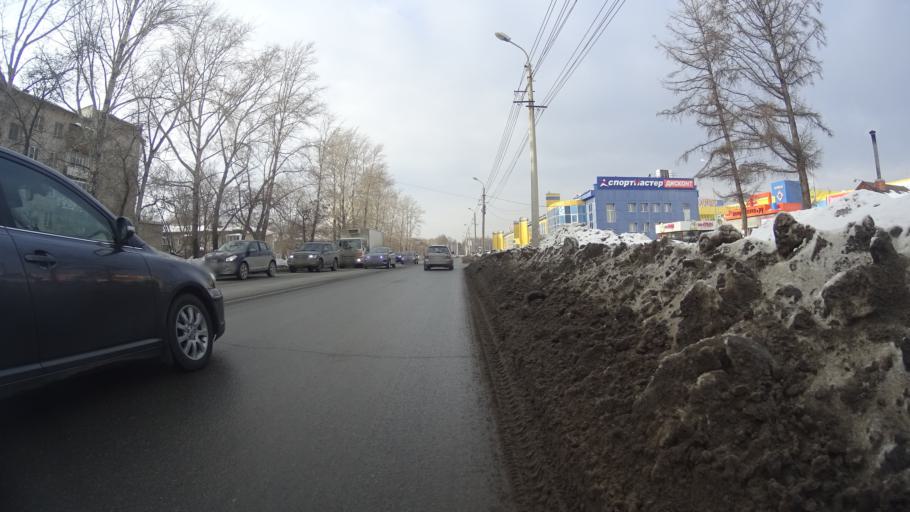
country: RU
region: Chelyabinsk
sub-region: Gorod Chelyabinsk
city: Chelyabinsk
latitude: 55.1254
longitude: 61.3699
